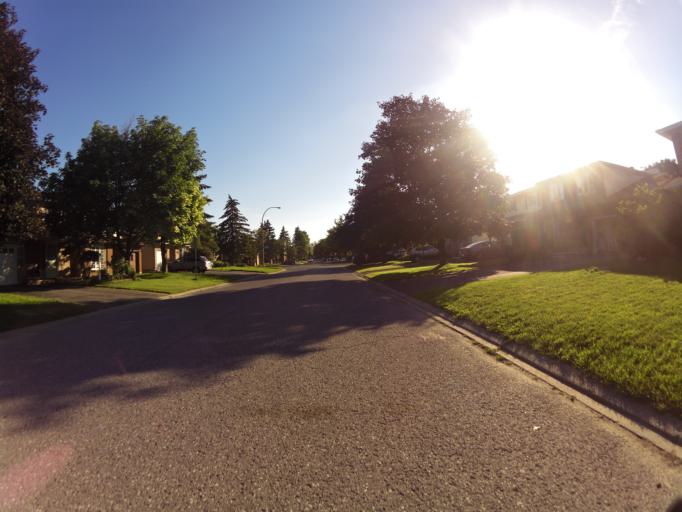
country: CA
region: Ontario
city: Bells Corners
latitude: 45.3341
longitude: -75.7562
